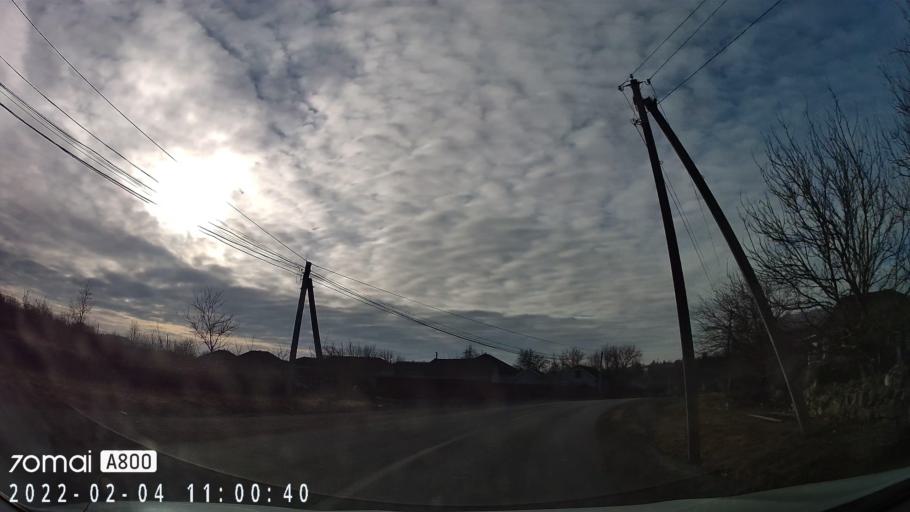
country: RO
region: Botosani
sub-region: Comuna Radauti-Prut
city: Miorcani
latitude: 48.2986
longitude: 26.9399
